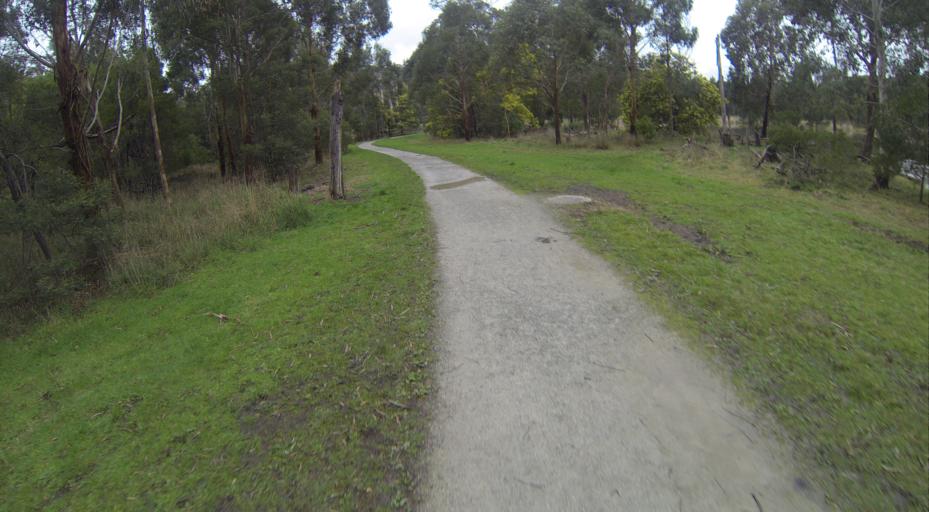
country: AU
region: Victoria
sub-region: Yarra Ranges
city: Belgrave South
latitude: -37.9235
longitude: 145.3266
